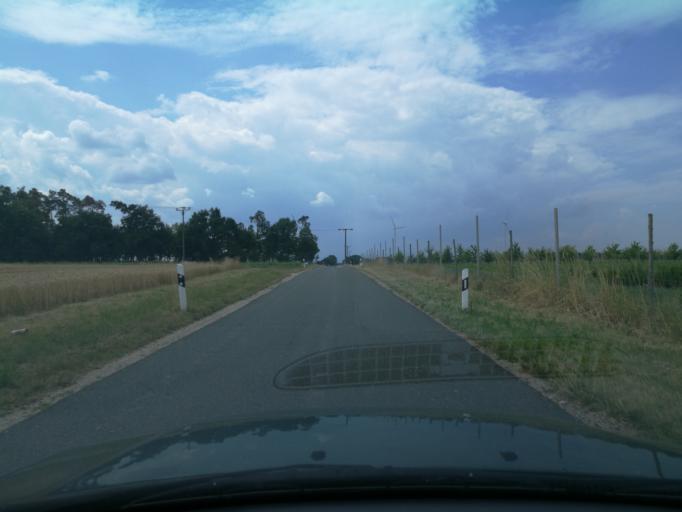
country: DE
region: Bavaria
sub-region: Regierungsbezirk Mittelfranken
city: Grosshabersdorf
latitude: 49.4365
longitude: 10.7894
